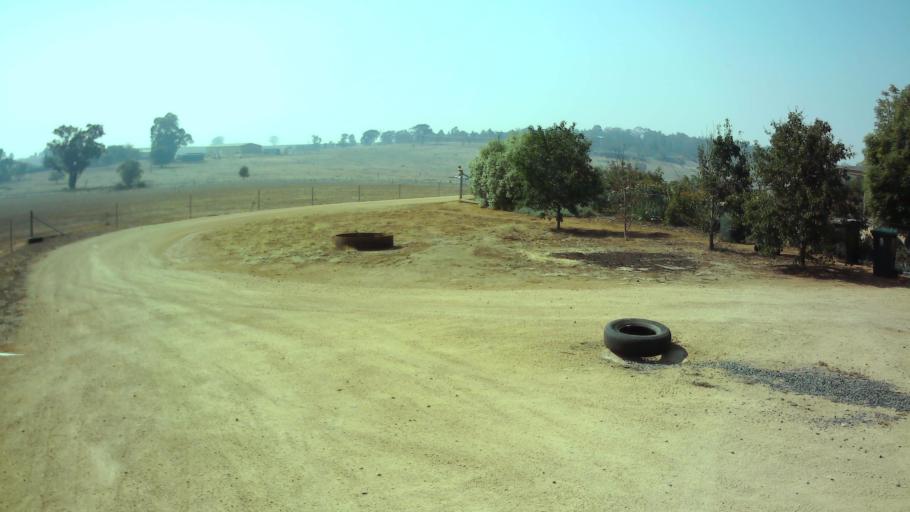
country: AU
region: New South Wales
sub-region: Weddin
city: Grenfell
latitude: -33.8972
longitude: 148.1795
